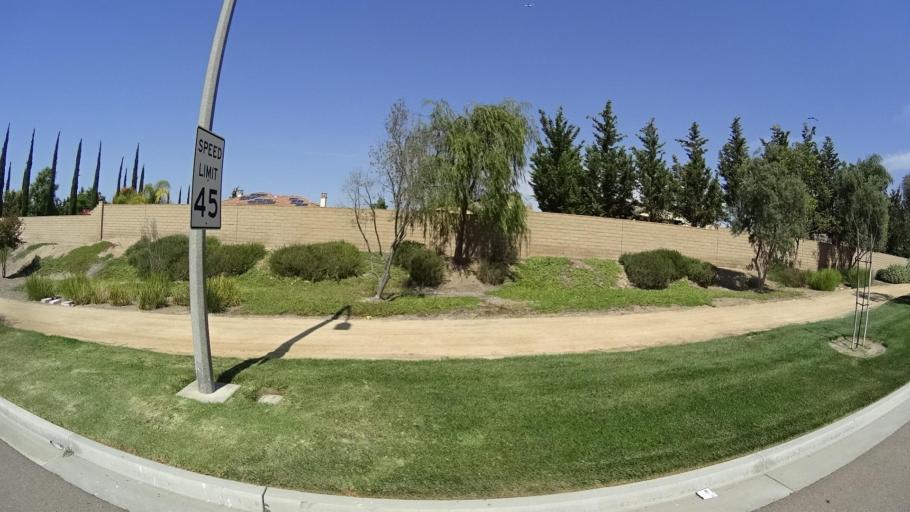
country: US
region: California
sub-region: San Diego County
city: La Presa
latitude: 32.6726
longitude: -116.9949
